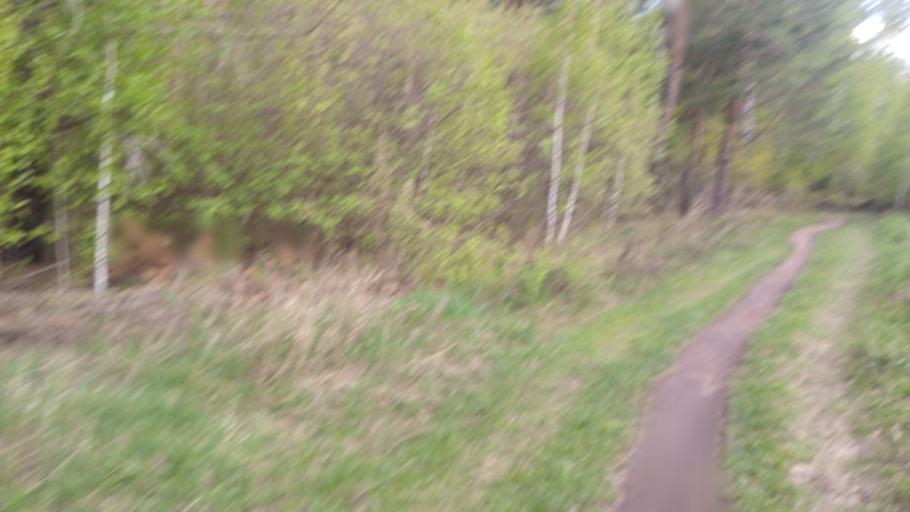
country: RU
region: Chelyabinsk
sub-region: Gorod Chelyabinsk
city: Chelyabinsk
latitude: 55.1644
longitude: 61.3156
